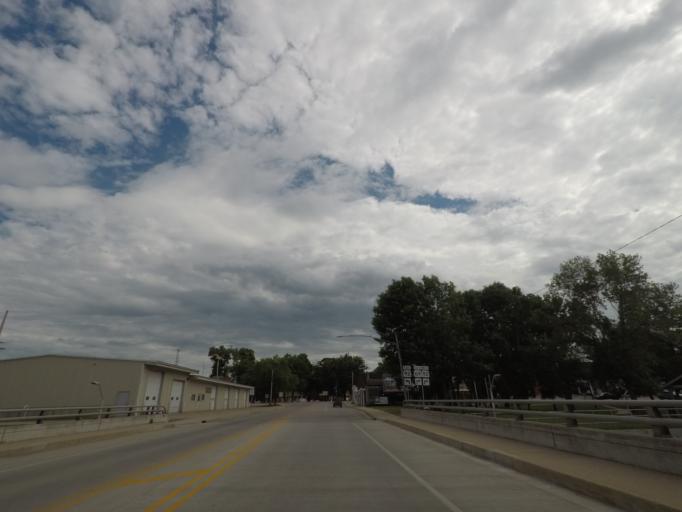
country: US
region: Wisconsin
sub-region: Dane County
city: Belleville
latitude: 42.8609
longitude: -89.5333
